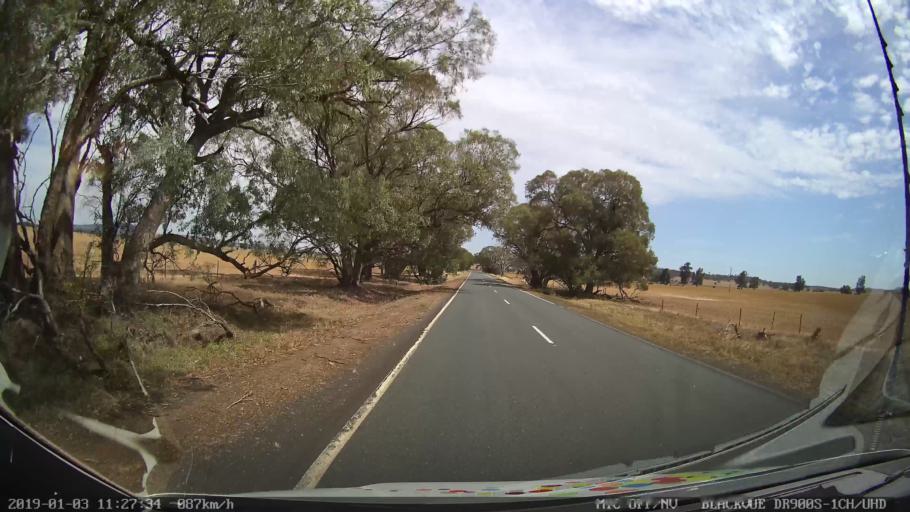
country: AU
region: New South Wales
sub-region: Weddin
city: Grenfell
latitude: -34.0110
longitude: 148.2179
